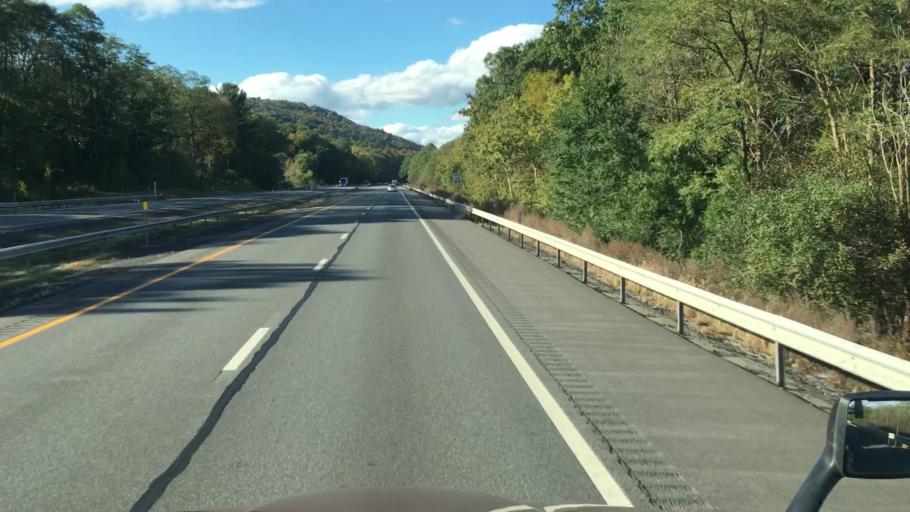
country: US
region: New York
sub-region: Schenectady County
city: Scotia
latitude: 42.8482
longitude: -74.0237
